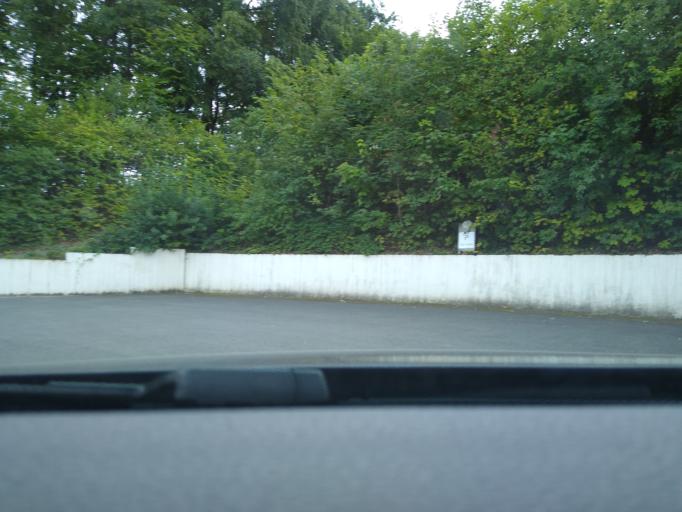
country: DE
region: Bavaria
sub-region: Upper Franconia
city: Obertrubach
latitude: 49.7077
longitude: 11.3728
